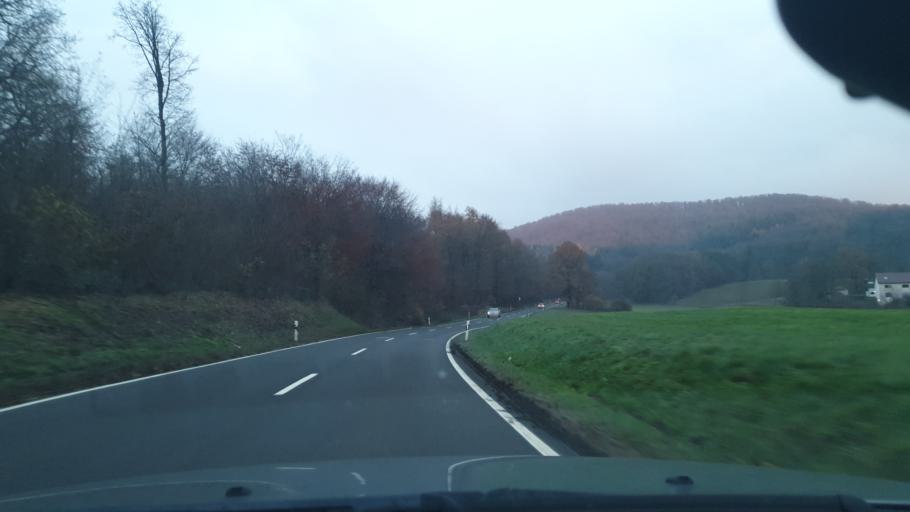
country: DE
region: Rheinland-Pfalz
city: Langwieden
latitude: 49.3840
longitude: 7.5178
